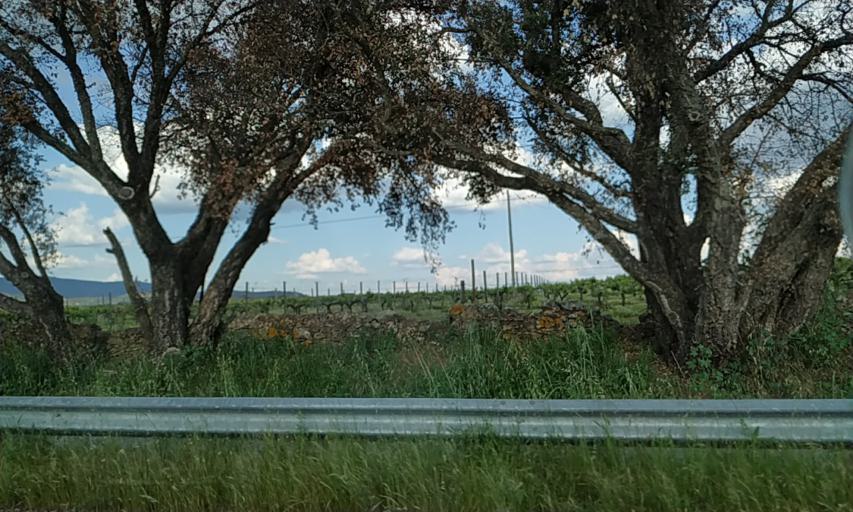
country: PT
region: Portalegre
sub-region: Portalegre
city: Portalegre
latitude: 39.2458
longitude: -7.4496
